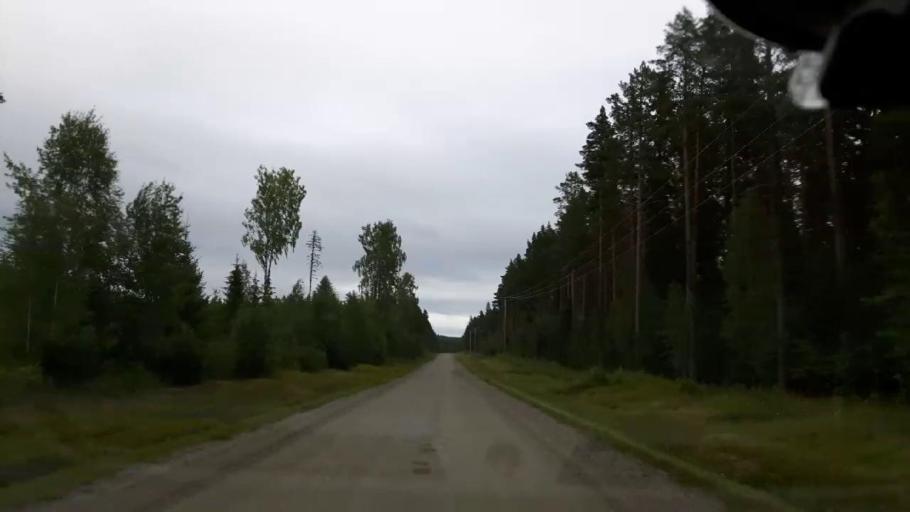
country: SE
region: Vaesternorrland
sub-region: Ange Kommun
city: Fransta
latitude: 62.8586
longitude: 15.9969
